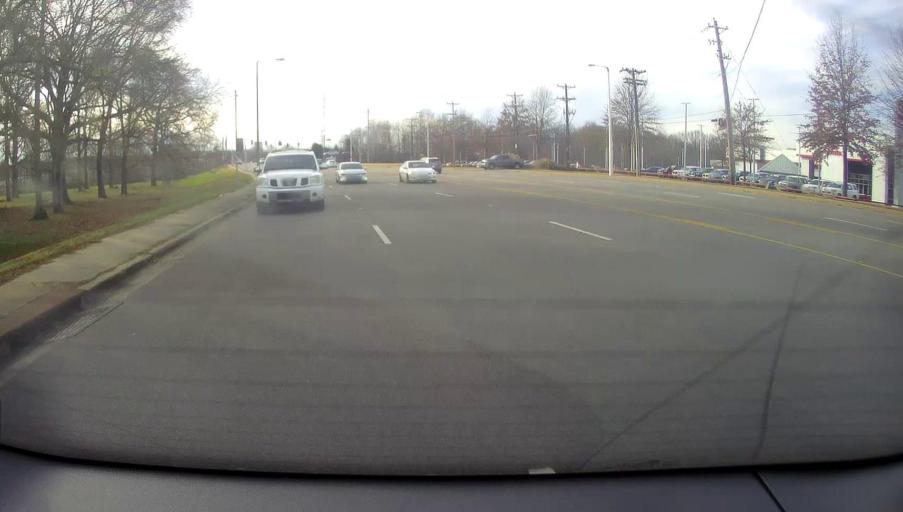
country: US
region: Tennessee
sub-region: Shelby County
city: Germantown
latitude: 35.0506
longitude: -89.8163
